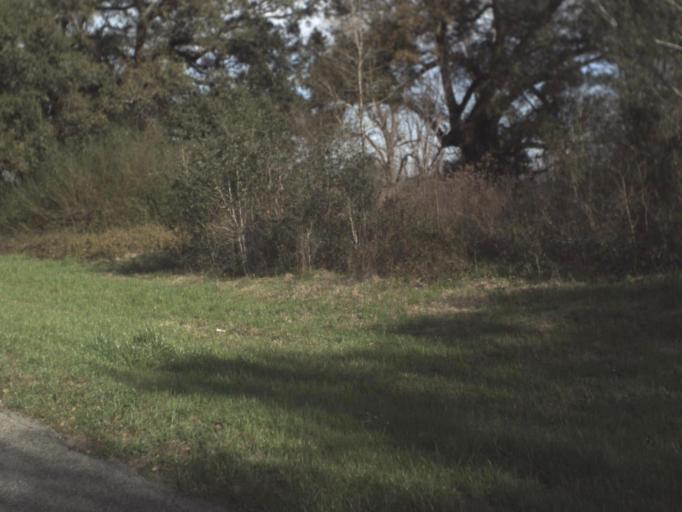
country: US
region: Florida
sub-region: Jackson County
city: Malone
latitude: 30.9891
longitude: -85.1903
